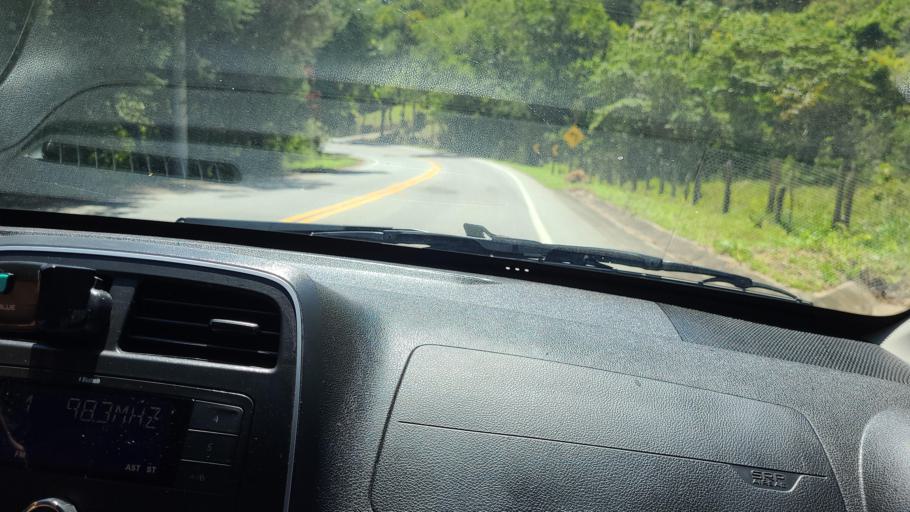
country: BR
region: Sao Paulo
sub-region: Tremembe
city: Tremembe
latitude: -22.8793
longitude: -45.5726
